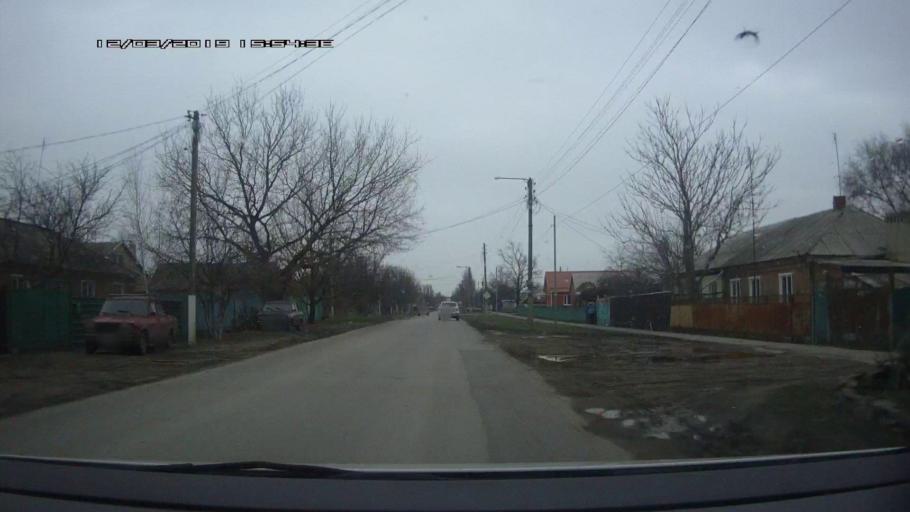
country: RU
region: Rostov
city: Novobataysk
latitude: 46.8918
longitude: 39.7780
